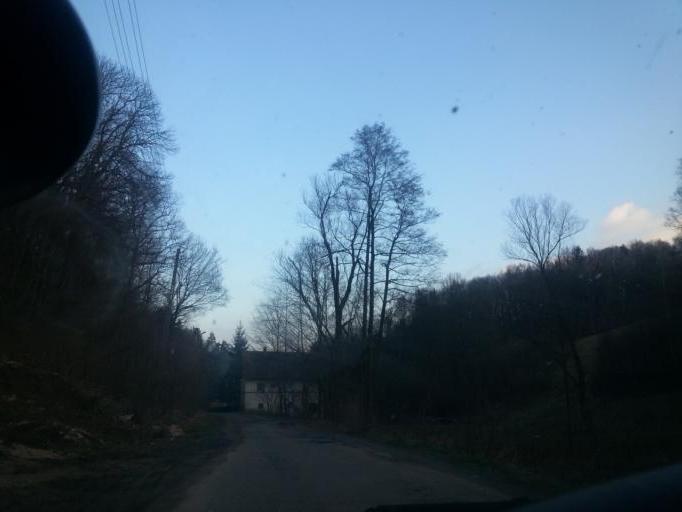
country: PL
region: Lower Silesian Voivodeship
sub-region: Powiat jeleniogorski
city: Stara Kamienica
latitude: 50.9704
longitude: 15.6177
